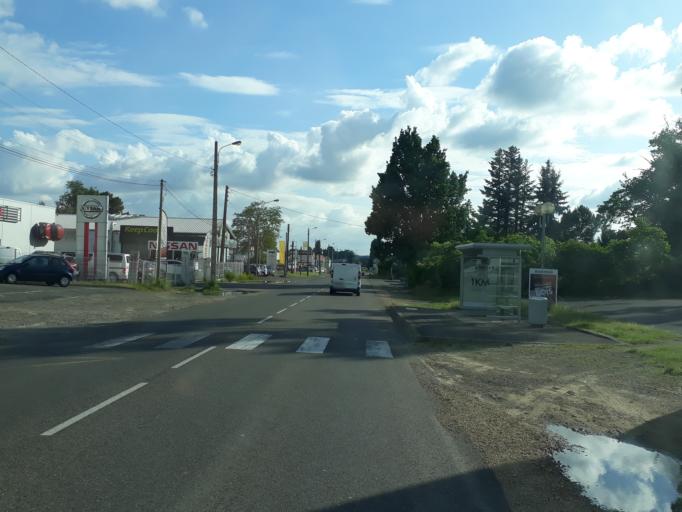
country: FR
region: Aquitaine
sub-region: Departement des Landes
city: Mont-de-Marsan
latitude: 43.9044
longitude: -0.4764
